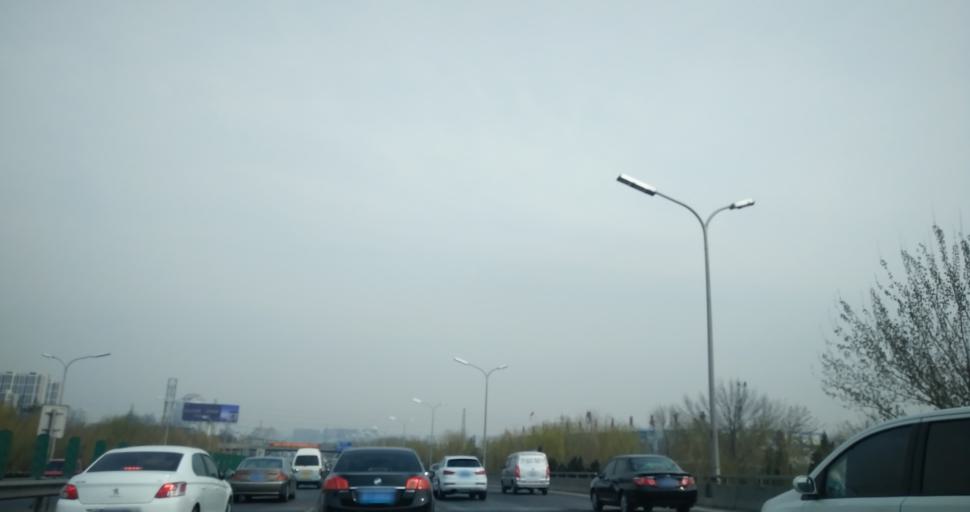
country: CN
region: Beijing
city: Jiugong
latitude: 39.8483
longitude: 116.4792
